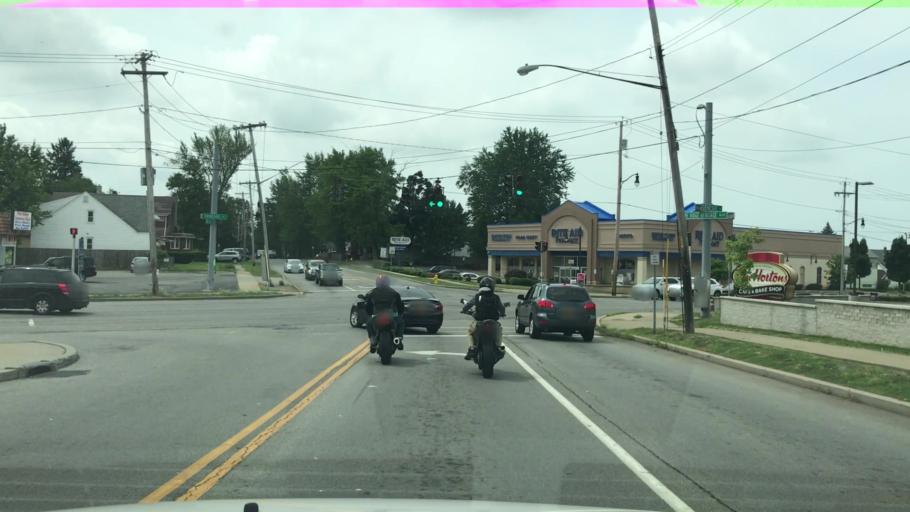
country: US
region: New York
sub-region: Erie County
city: Sloan
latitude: 42.9202
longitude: -78.7935
